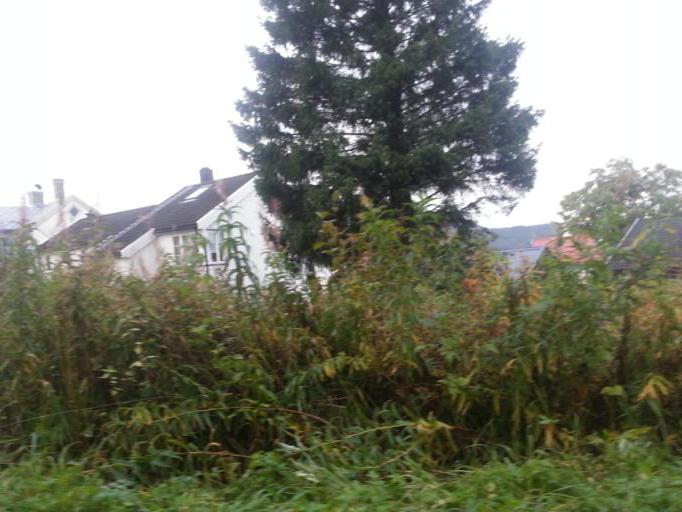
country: NO
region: Sor-Trondelag
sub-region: Trondheim
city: Trondheim
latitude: 63.4295
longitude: 10.4096
